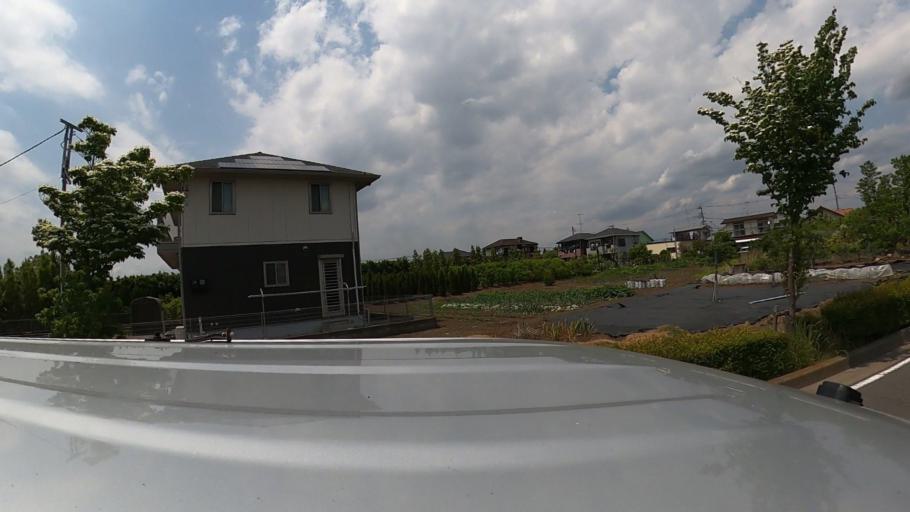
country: JP
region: Kanagawa
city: Chigasaki
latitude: 35.3923
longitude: 139.4072
